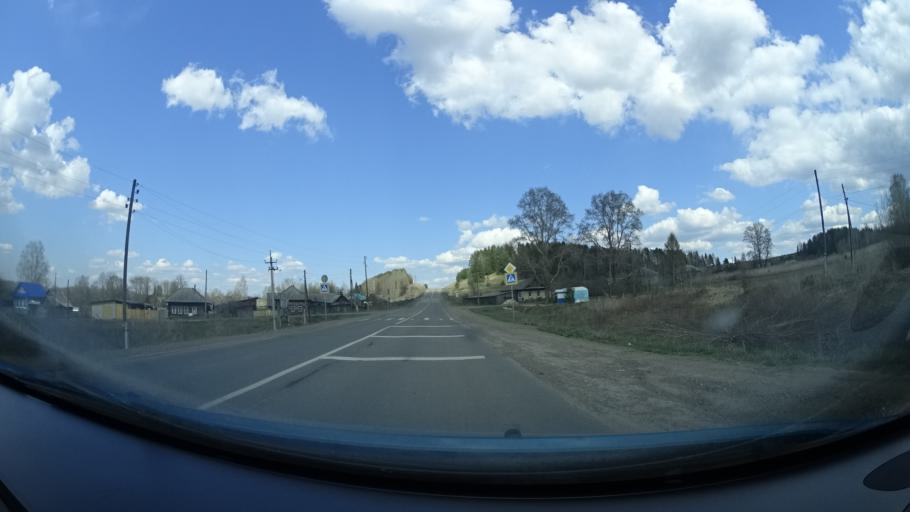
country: RU
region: Perm
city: Osa
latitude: 57.1885
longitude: 55.5910
